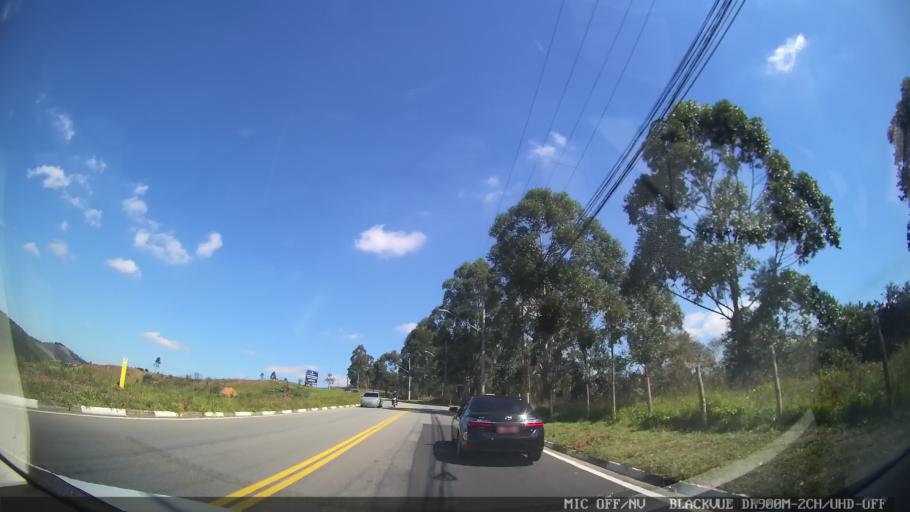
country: BR
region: Sao Paulo
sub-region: Barueri
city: Barueri
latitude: -23.4460
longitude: -46.8364
